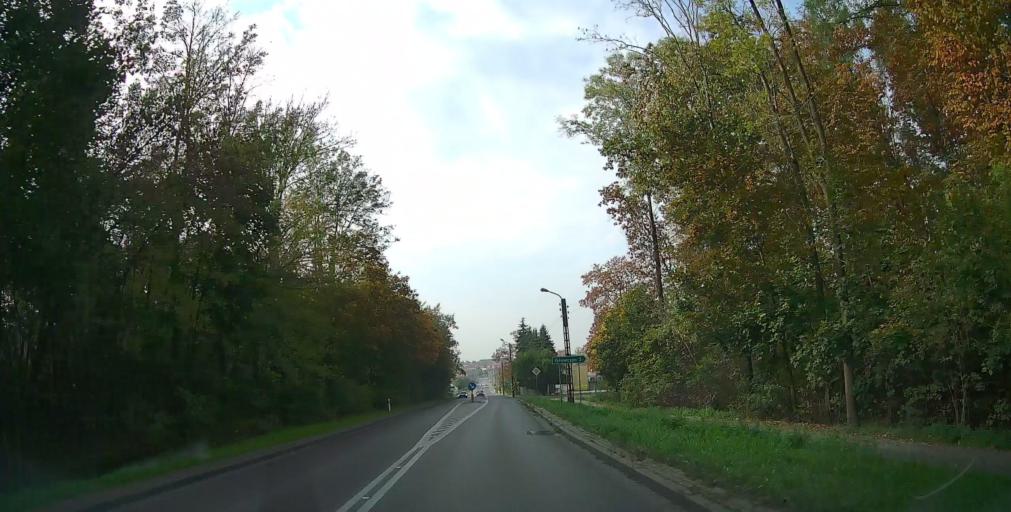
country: PL
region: Masovian Voivodeship
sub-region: Powiat grojecki
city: Mogielnica
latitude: 51.6982
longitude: 20.7287
